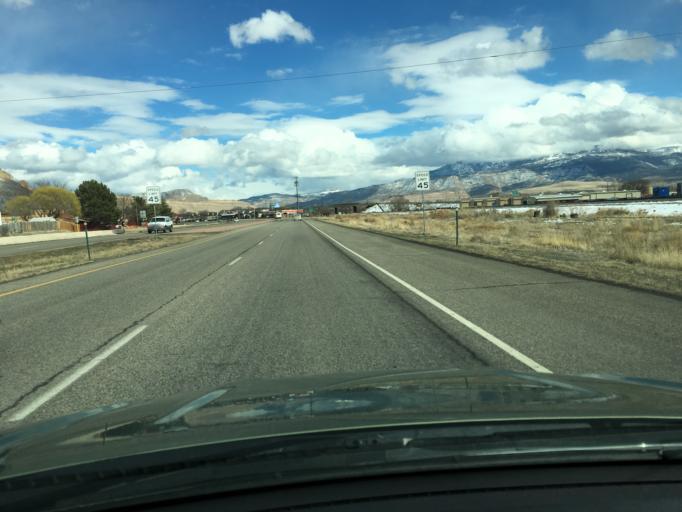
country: US
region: Colorado
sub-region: Mesa County
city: Clifton
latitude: 39.0849
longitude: -108.4644
